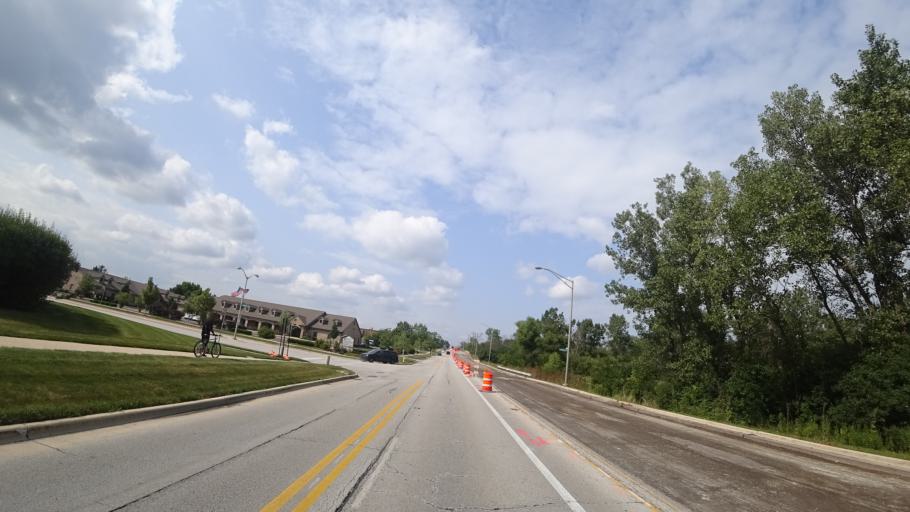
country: US
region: Illinois
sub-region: Cook County
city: Tinley Park
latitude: 41.5973
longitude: -87.7852
